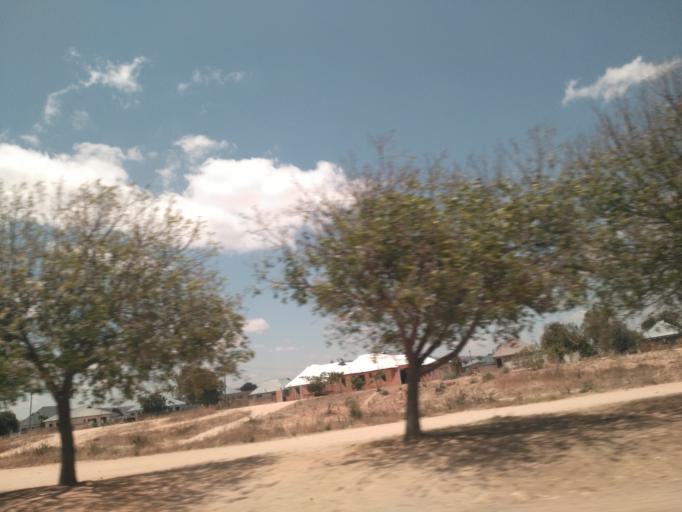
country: TZ
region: Dodoma
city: Kisasa
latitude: -6.1718
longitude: 35.7702
